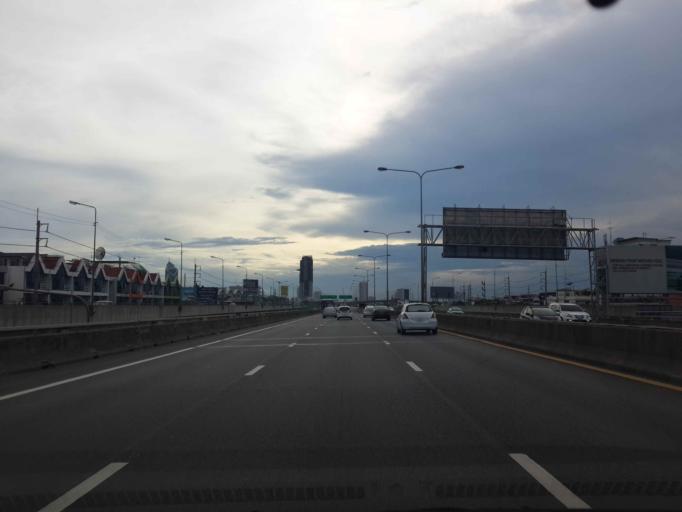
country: TH
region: Bangkok
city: Yan Nawa
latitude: 13.6961
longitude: 100.5361
